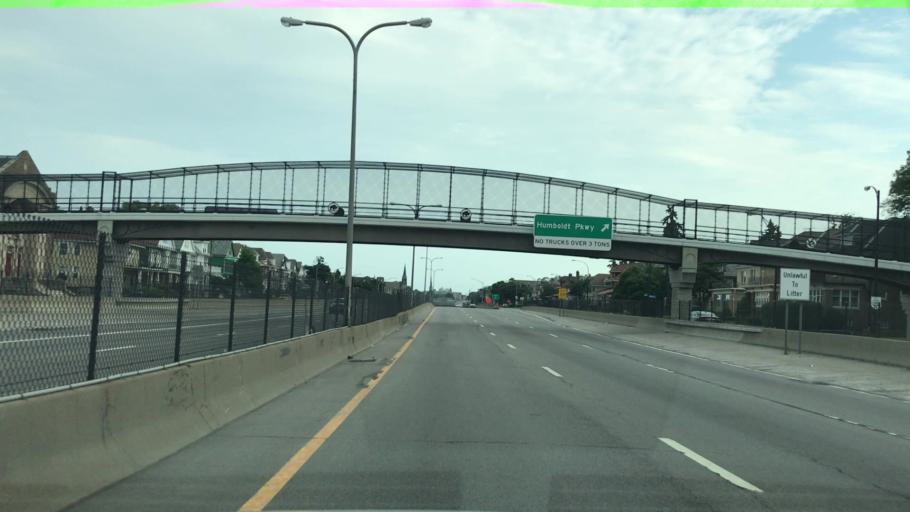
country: US
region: New York
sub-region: Erie County
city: Buffalo
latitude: 42.9188
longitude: -78.8435
